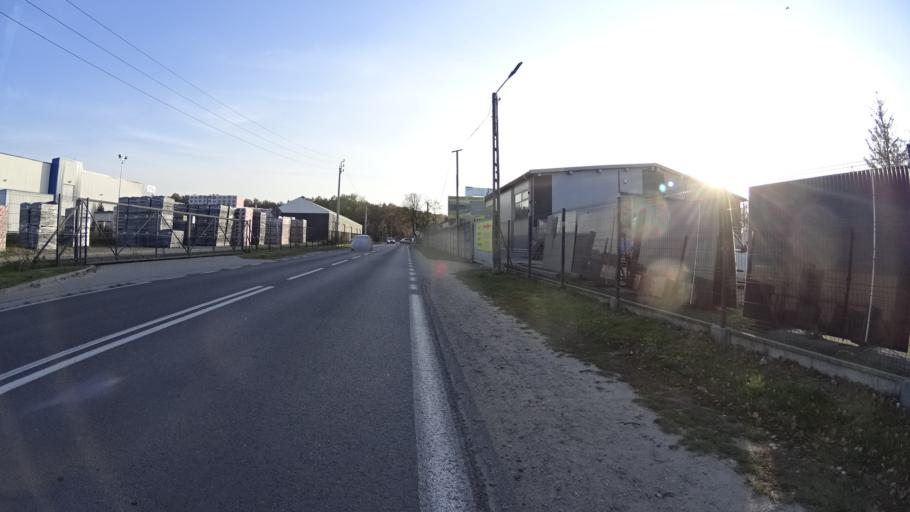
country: PL
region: Masovian Voivodeship
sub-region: Powiat warszawski zachodni
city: Babice
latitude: 52.2777
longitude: 20.8662
